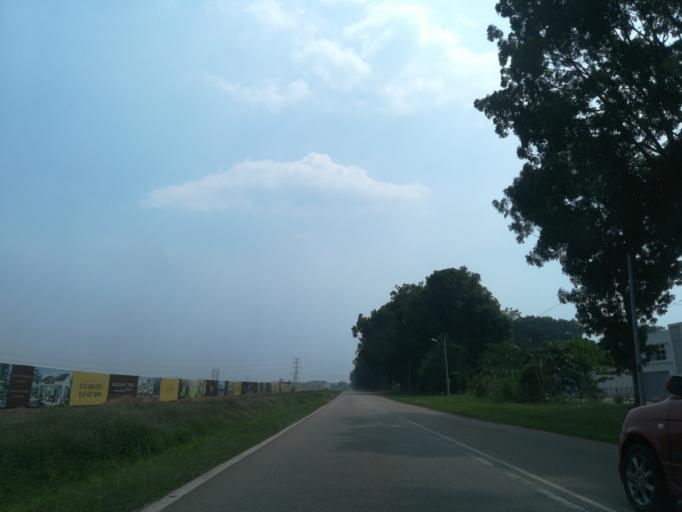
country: MY
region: Penang
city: Tasek Glugor
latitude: 5.4465
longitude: 100.5384
